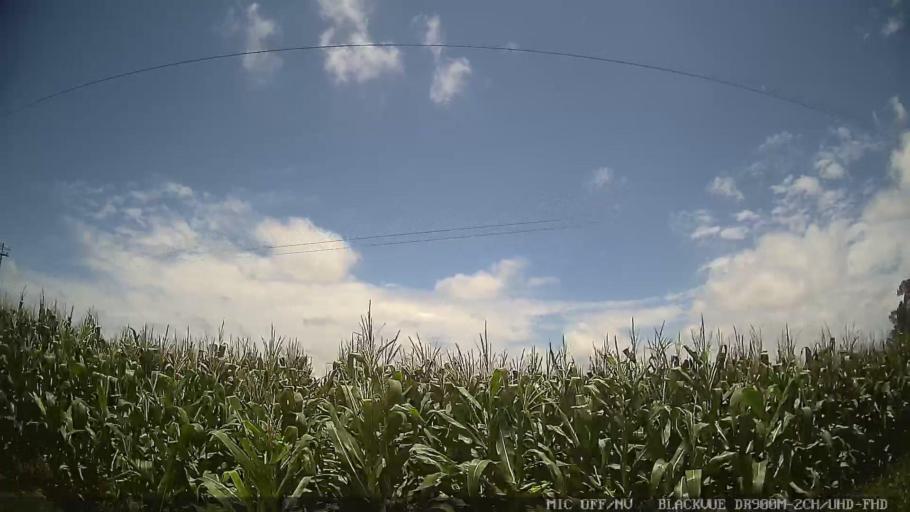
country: BR
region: Sao Paulo
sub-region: Laranjal Paulista
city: Laranjal Paulista
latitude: -23.0269
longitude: -47.8578
